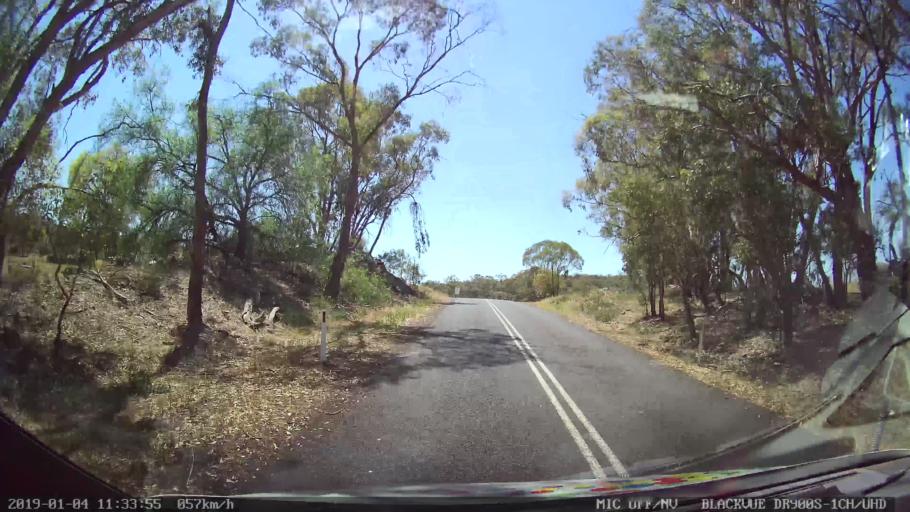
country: AU
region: New South Wales
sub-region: Cabonne
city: Molong
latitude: -33.0664
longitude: 148.8228
